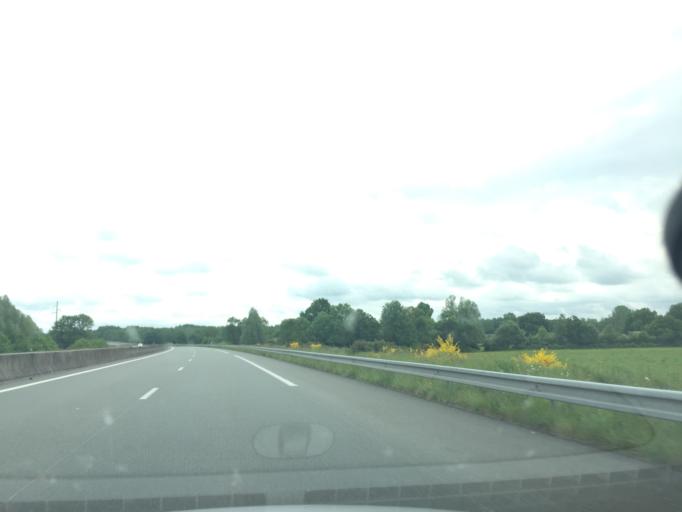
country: FR
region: Pays de la Loire
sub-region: Departement de la Sarthe
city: Luceau
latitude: 47.6670
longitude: 0.3762
